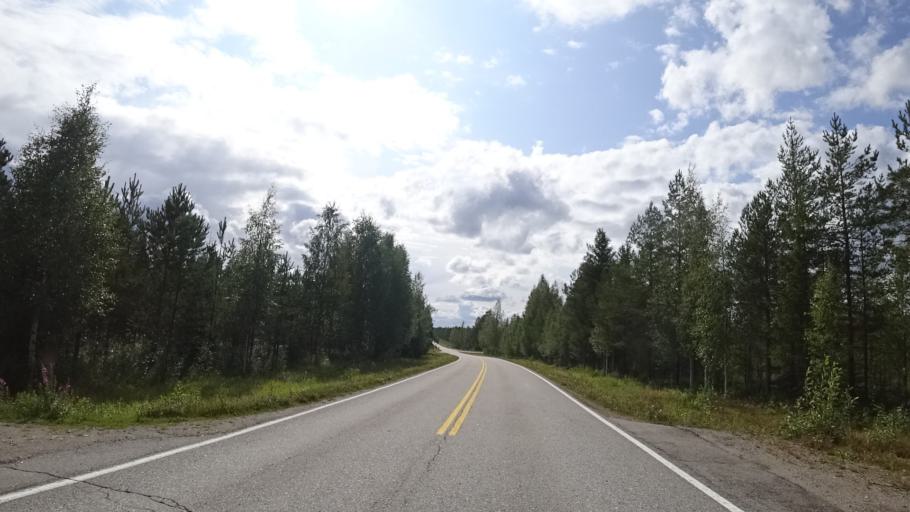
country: FI
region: North Karelia
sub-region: Joensuu
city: Ilomantsi
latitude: 62.7677
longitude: 31.0366
